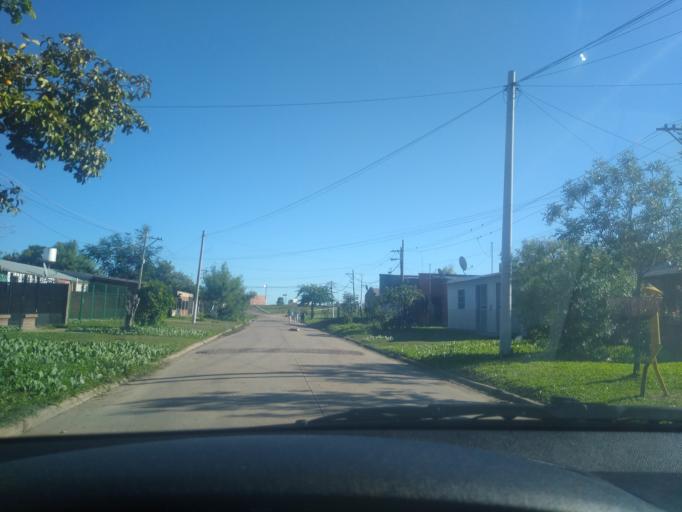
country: AR
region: Chaco
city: Puerto Vilelas
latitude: -27.5048
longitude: -58.9414
